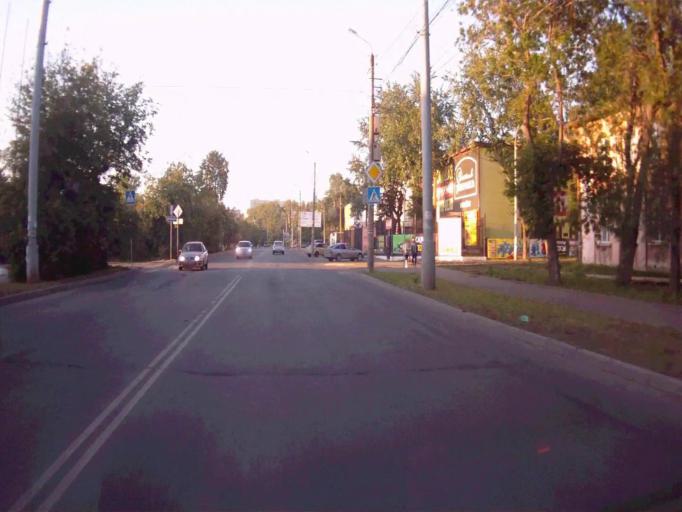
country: RU
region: Chelyabinsk
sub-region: Gorod Chelyabinsk
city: Chelyabinsk
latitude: 55.1654
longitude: 61.4345
